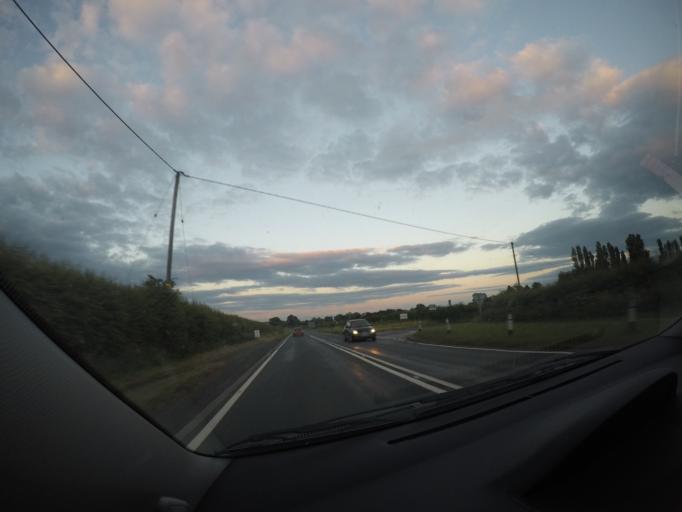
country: GB
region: England
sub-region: City and Borough of Leeds
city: Wetherby
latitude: 54.0092
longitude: -1.3590
